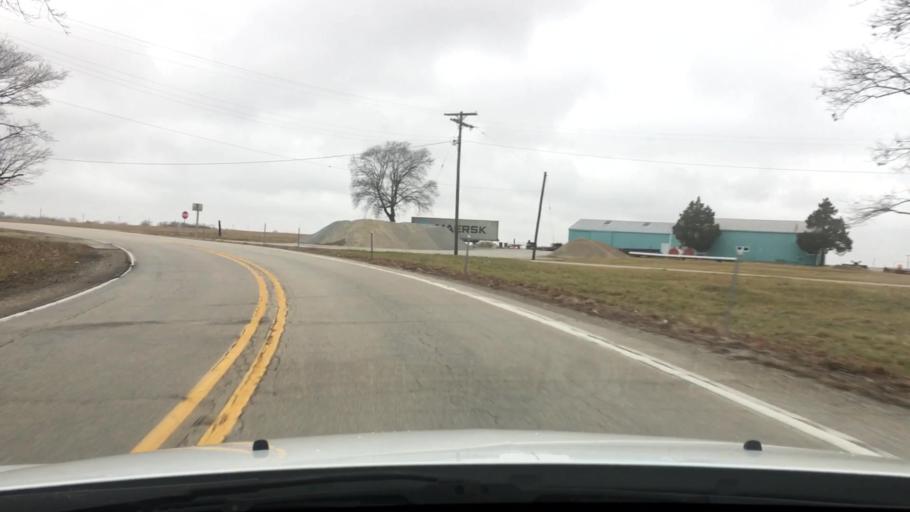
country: US
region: Illinois
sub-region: Iroquois County
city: Sheldon
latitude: 40.8287
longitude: -87.5820
